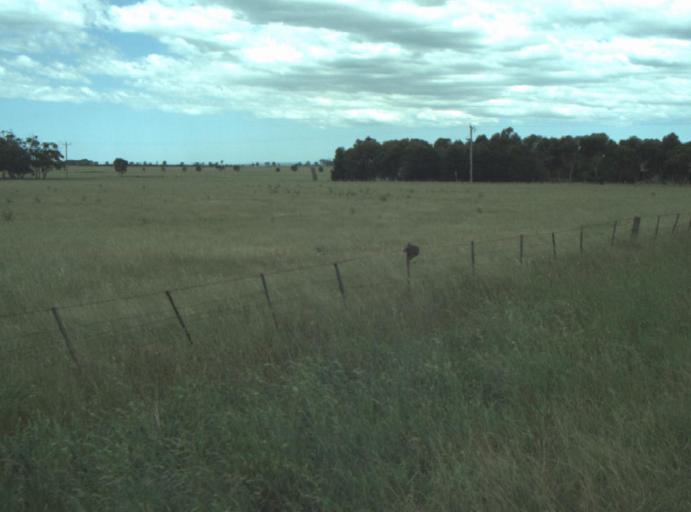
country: AU
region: Victoria
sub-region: Wyndham
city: Little River
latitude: -37.9557
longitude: 144.4643
